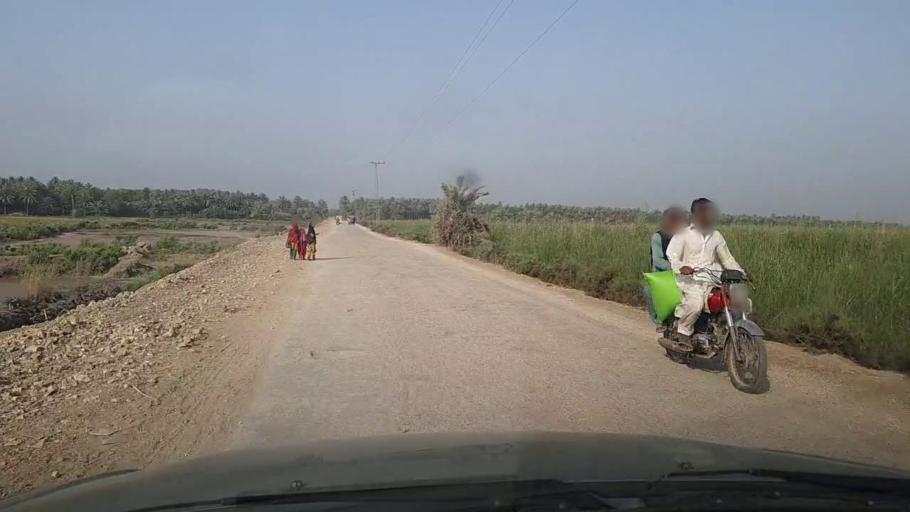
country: PK
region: Sindh
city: Pir jo Goth
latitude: 27.5629
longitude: 68.5704
